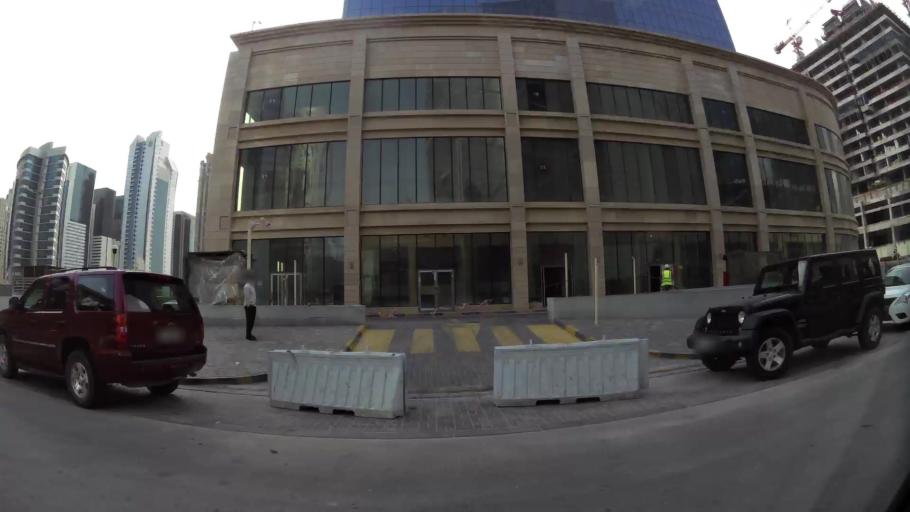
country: QA
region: Baladiyat ad Dawhah
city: Doha
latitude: 25.3221
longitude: 51.5261
